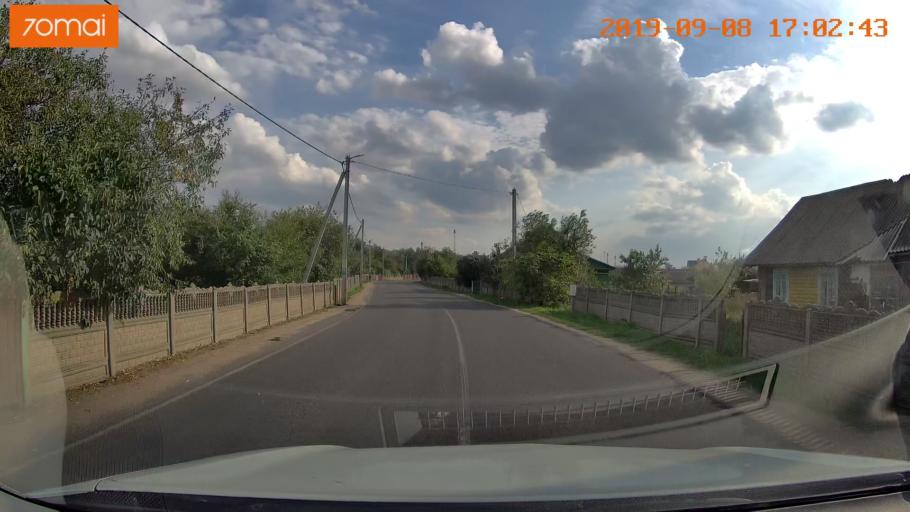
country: BY
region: Grodnenskaya
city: Hrodna
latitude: 53.7010
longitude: 23.9402
